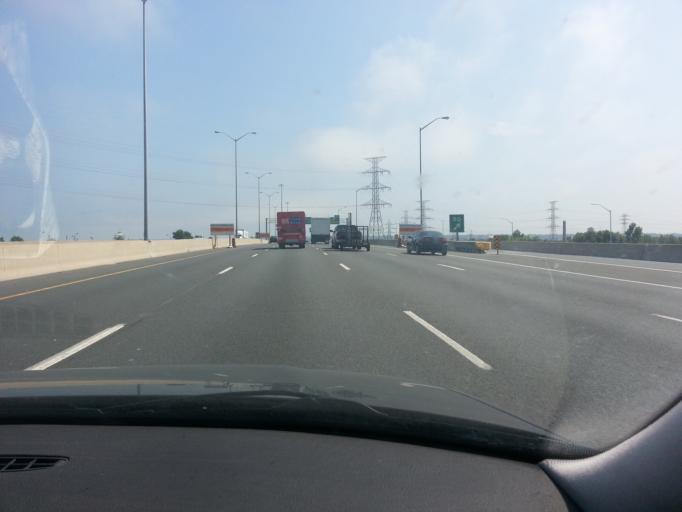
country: CA
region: Ontario
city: Hamilton
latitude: 43.2655
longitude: -79.7742
